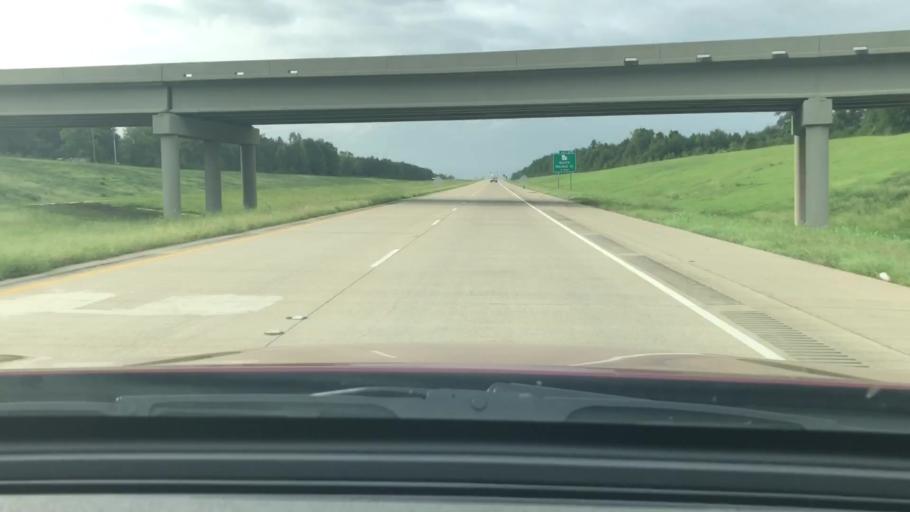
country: US
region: Louisiana
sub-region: Caddo Parish
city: Blanchard
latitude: 32.6168
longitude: -93.8354
